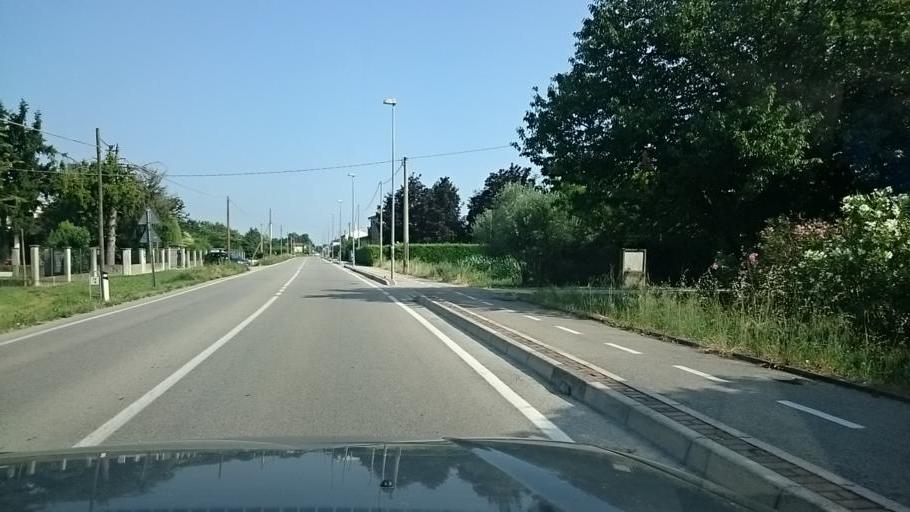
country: IT
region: Veneto
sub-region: Provincia di Padova
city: Saletto
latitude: 45.4675
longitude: 11.8666
